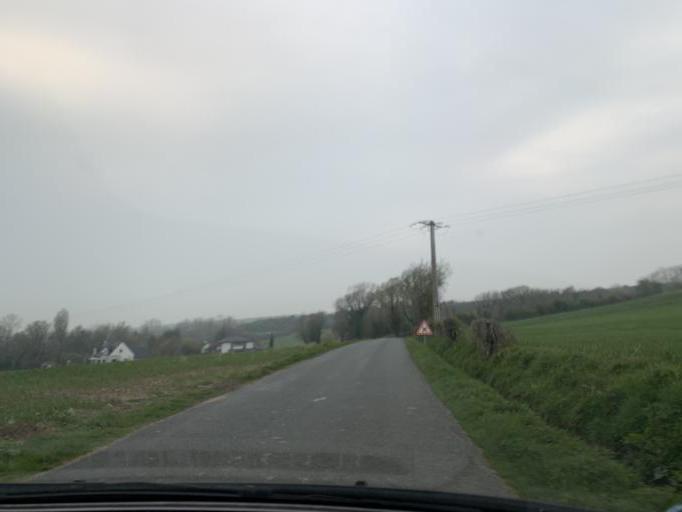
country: FR
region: Nord-Pas-de-Calais
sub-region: Departement du Pas-de-Calais
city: Wimille
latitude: 50.7601
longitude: 1.6659
